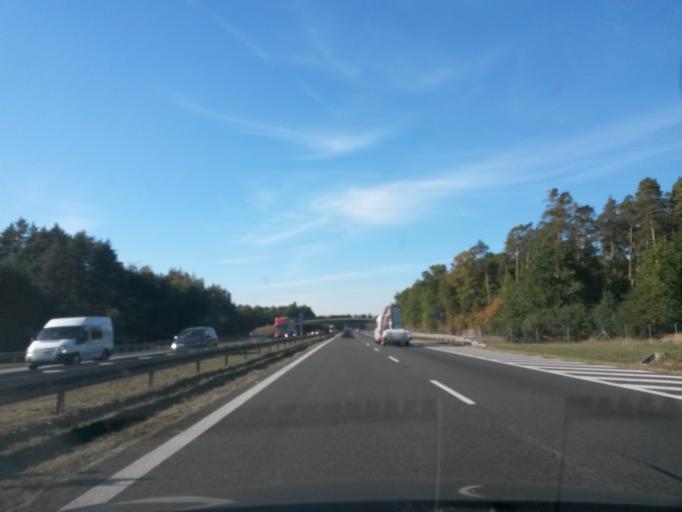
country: PL
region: Opole Voivodeship
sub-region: Powiat opolski
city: Niemodlin
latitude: 50.6839
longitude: 17.6414
